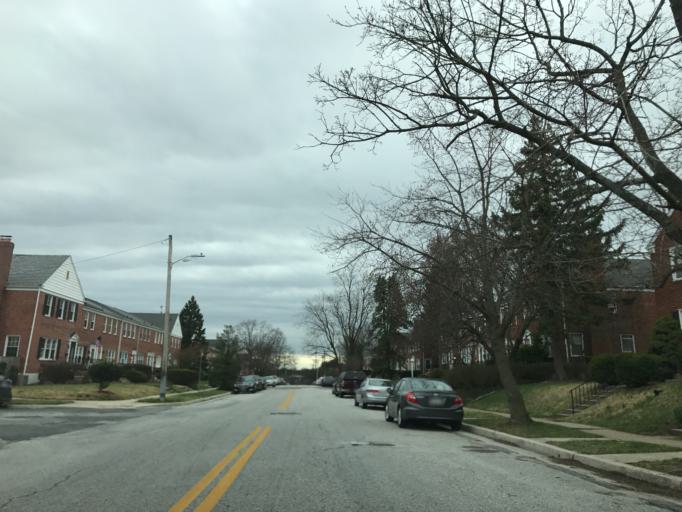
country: US
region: Maryland
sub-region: Baltimore County
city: Towson
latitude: 39.3894
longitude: -76.5751
